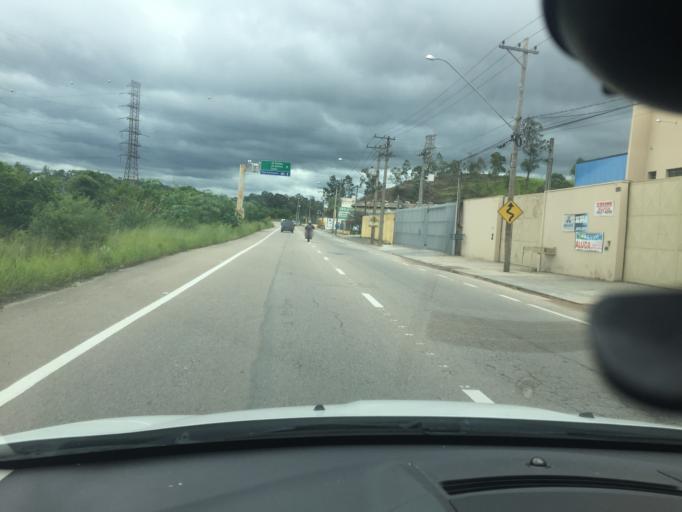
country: BR
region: Sao Paulo
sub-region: Varzea Paulista
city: Varzea Paulista
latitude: -23.2022
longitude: -46.8213
